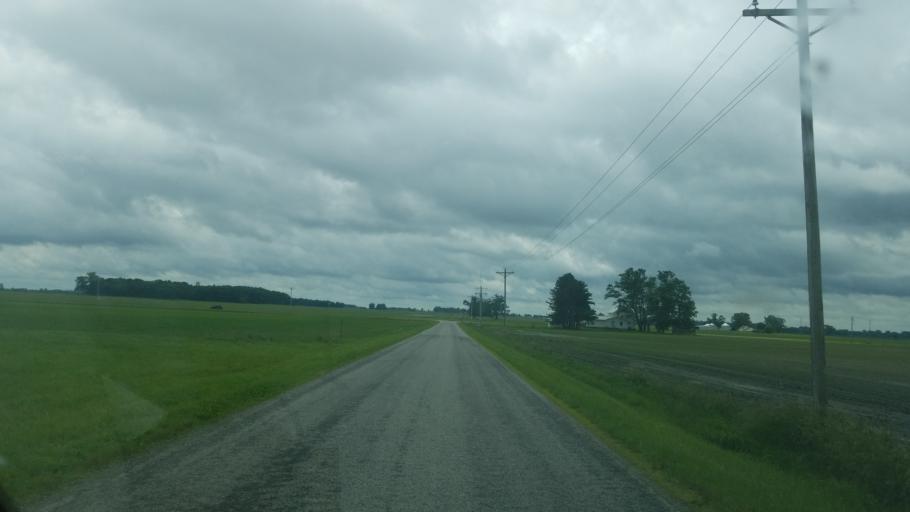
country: US
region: Ohio
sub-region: Marion County
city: Marion
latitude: 40.6765
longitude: -83.0686
